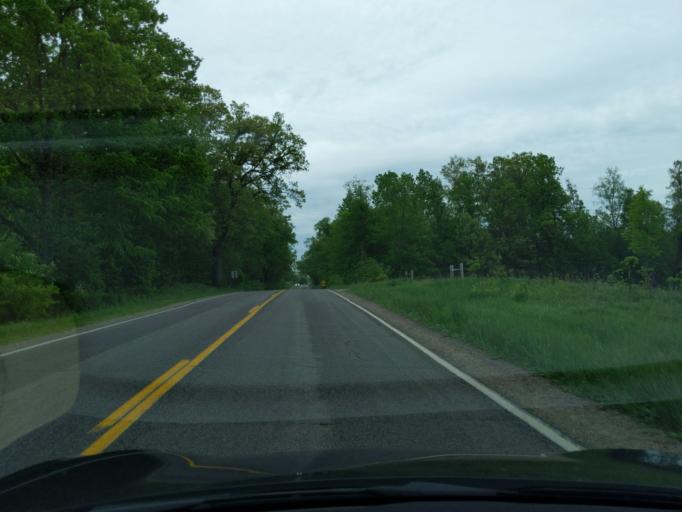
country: US
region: Michigan
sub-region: Ingham County
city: Leslie
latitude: 42.5067
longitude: -84.3563
